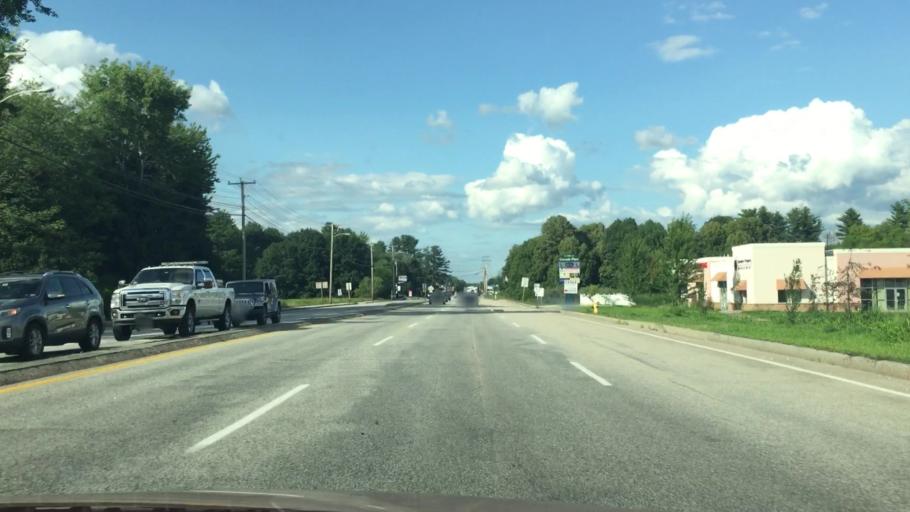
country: US
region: Maine
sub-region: Cumberland County
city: West Scarborough
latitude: 43.5466
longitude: -70.4121
